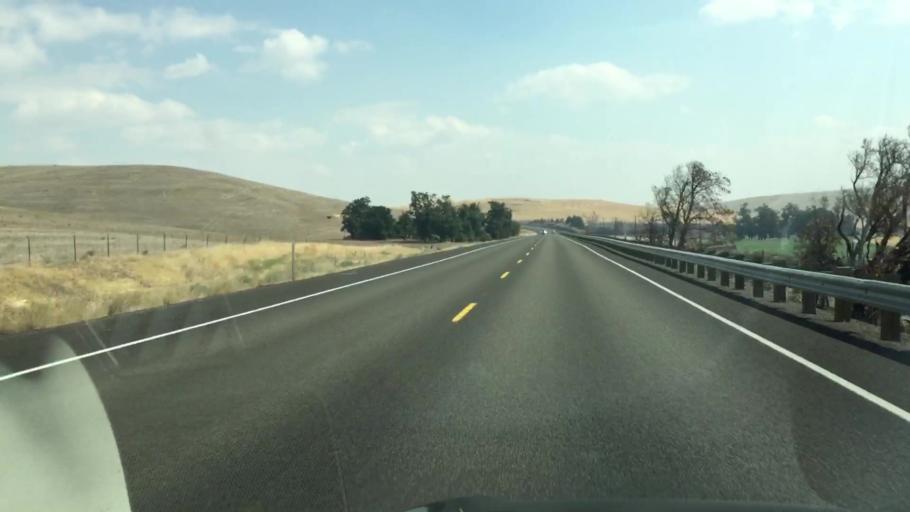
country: US
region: Oregon
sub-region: Wasco County
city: The Dalles
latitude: 45.4892
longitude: -121.1033
